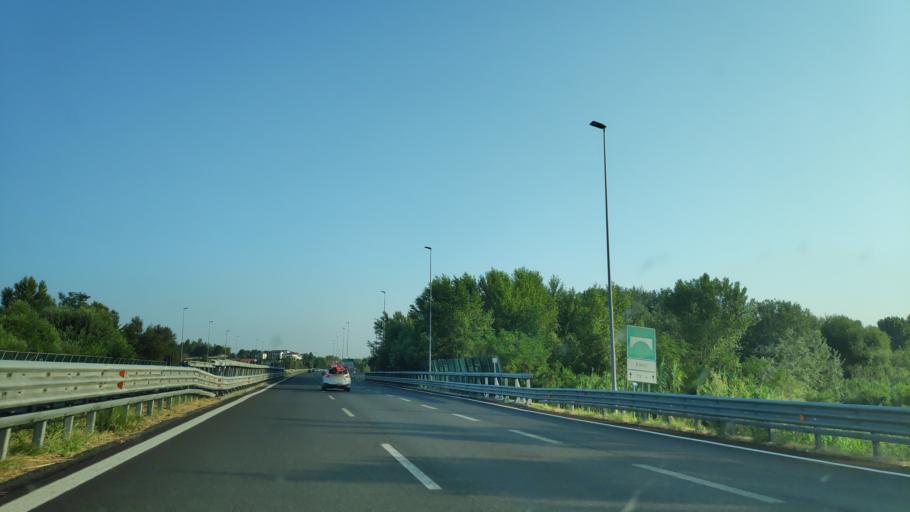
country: IT
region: Calabria
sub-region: Provincia di Cosenza
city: Quattromiglia
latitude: 39.3494
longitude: 16.2346
